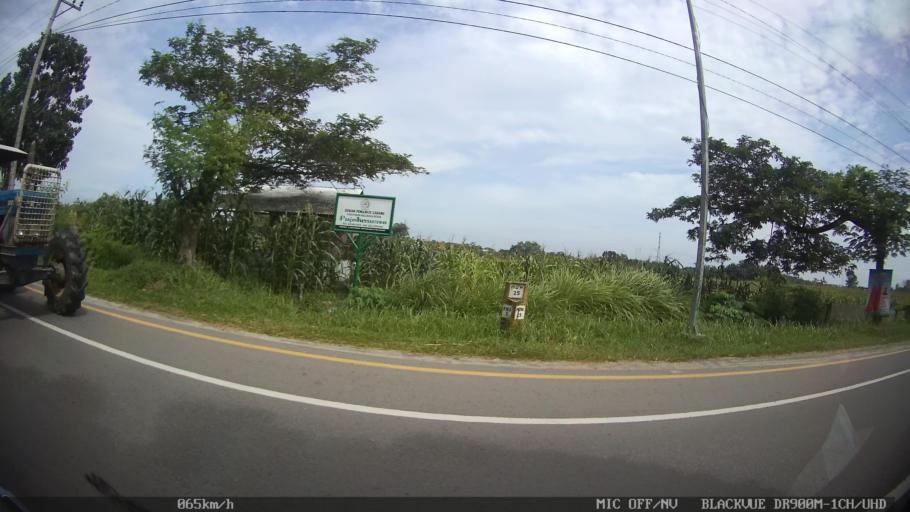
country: ID
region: North Sumatra
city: Percut
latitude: 3.5970
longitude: 98.8090
